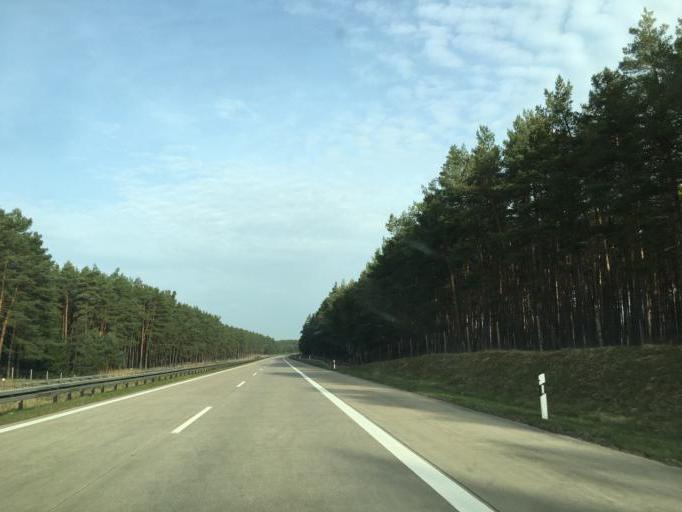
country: DE
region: Mecklenburg-Vorpommern
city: Plau am See
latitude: 53.5474
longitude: 12.3304
